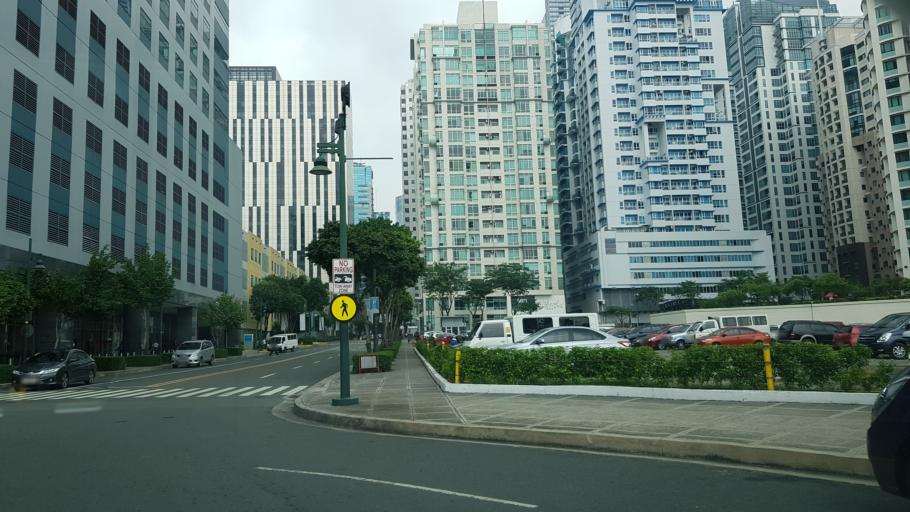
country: PH
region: Metro Manila
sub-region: Makati City
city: Makati City
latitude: 14.5550
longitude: 121.0427
